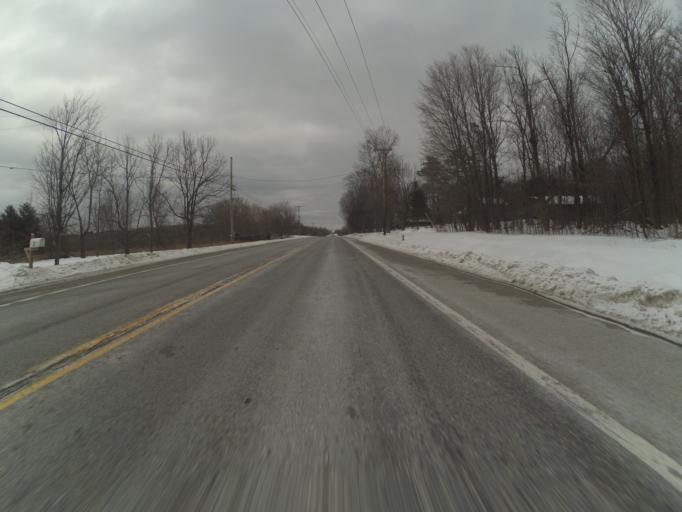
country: US
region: New York
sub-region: St. Lawrence County
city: Potsdam
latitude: 44.7052
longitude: -74.9326
